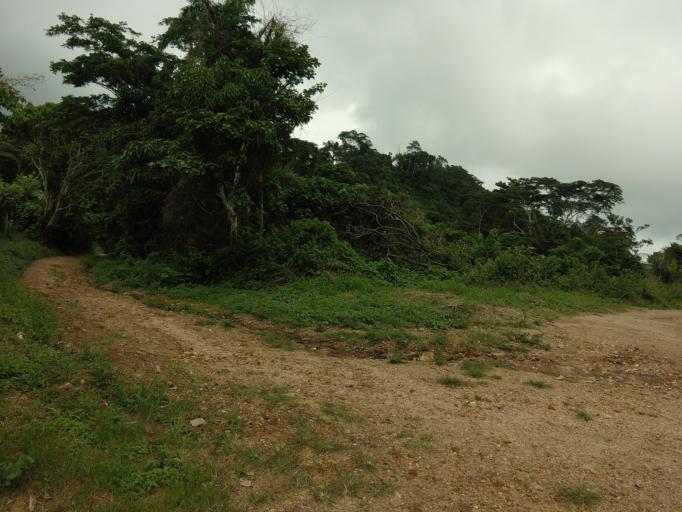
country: TG
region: Plateaux
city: Kpalime
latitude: 6.8446
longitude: 0.4408
